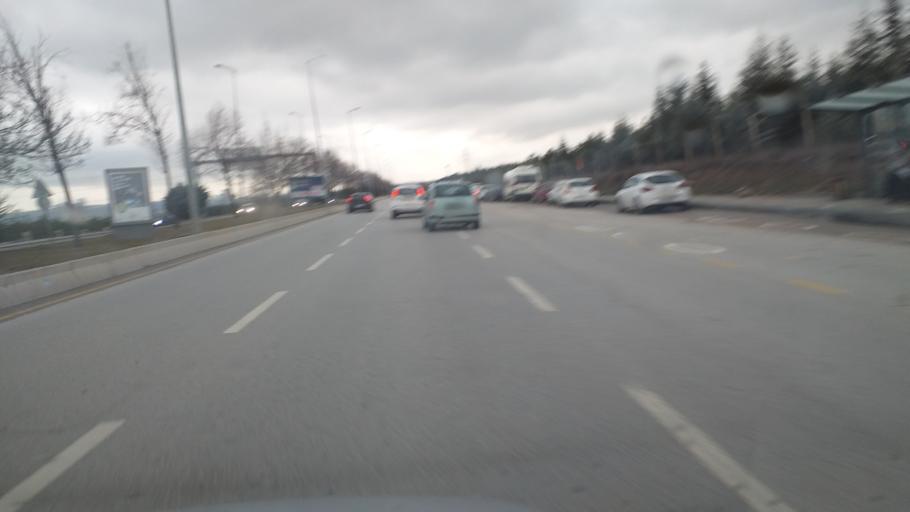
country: TR
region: Ankara
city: Batikent
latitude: 39.9044
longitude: 32.7327
